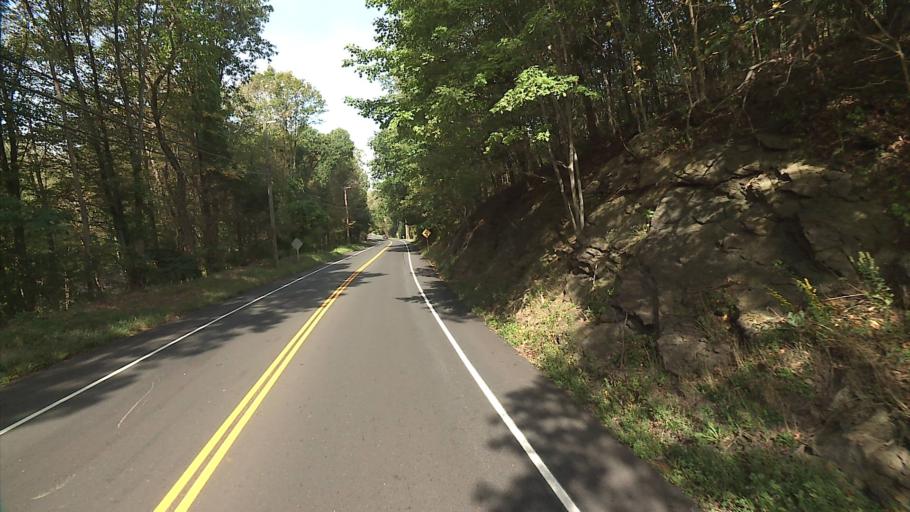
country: US
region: Connecticut
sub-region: Fairfield County
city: Newtown
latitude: 41.4018
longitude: -73.2486
